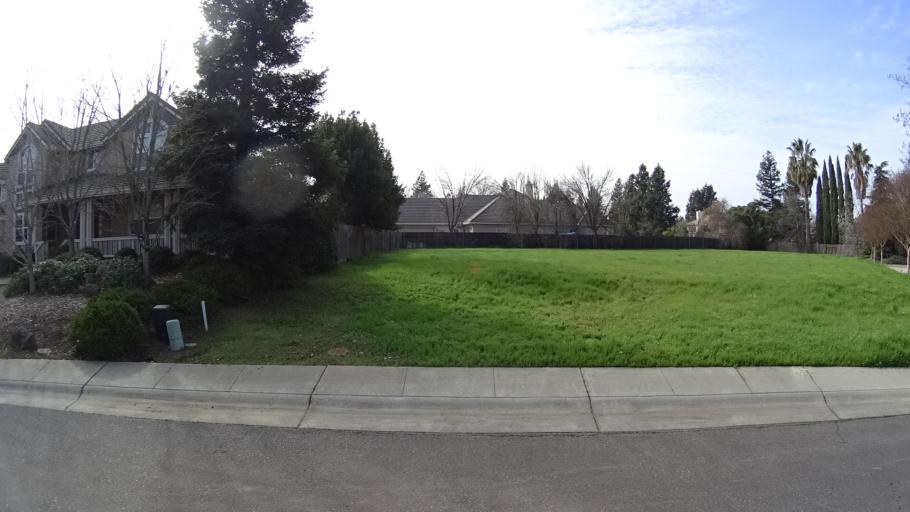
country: US
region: California
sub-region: Yolo County
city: Davis
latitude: 38.5398
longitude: -121.7145
